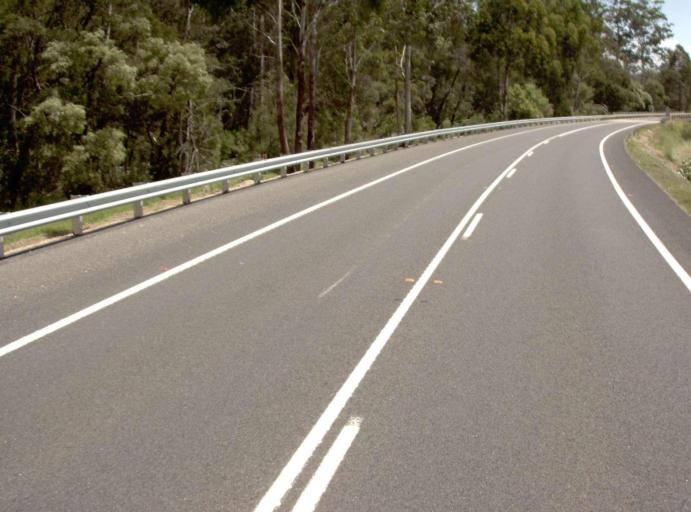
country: AU
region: New South Wales
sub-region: Bombala
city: Bombala
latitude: -37.5700
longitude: 149.1380
